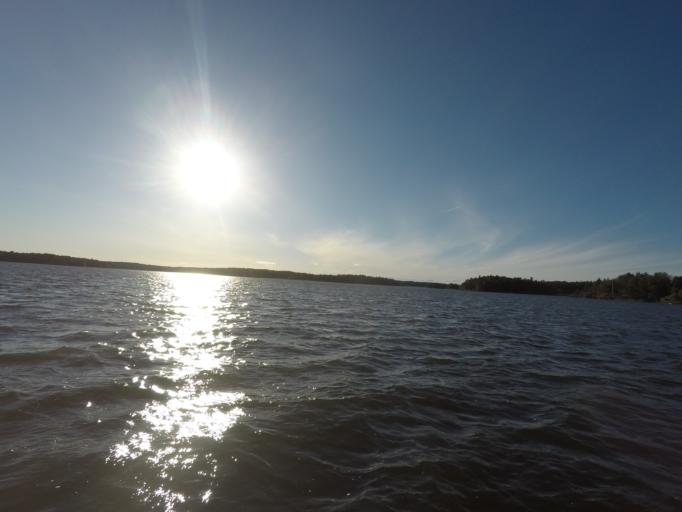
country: SE
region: Soedermanland
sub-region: Eskilstuna Kommun
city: Torshalla
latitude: 59.4714
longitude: 16.4402
